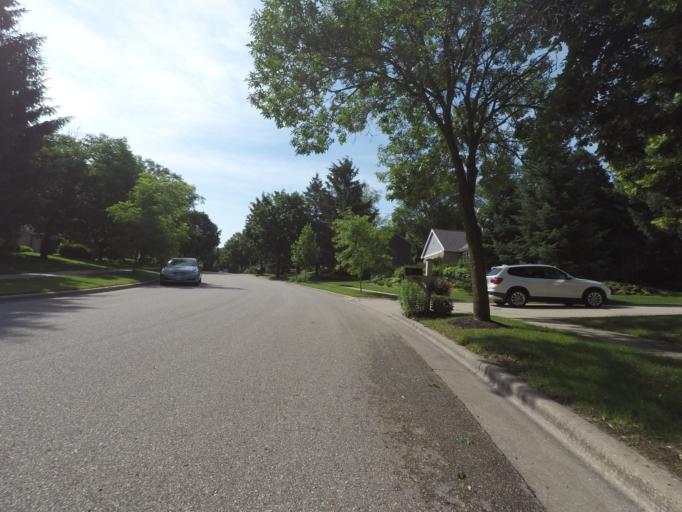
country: US
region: Wisconsin
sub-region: Dane County
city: Middleton
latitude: 43.0801
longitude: -89.4943
